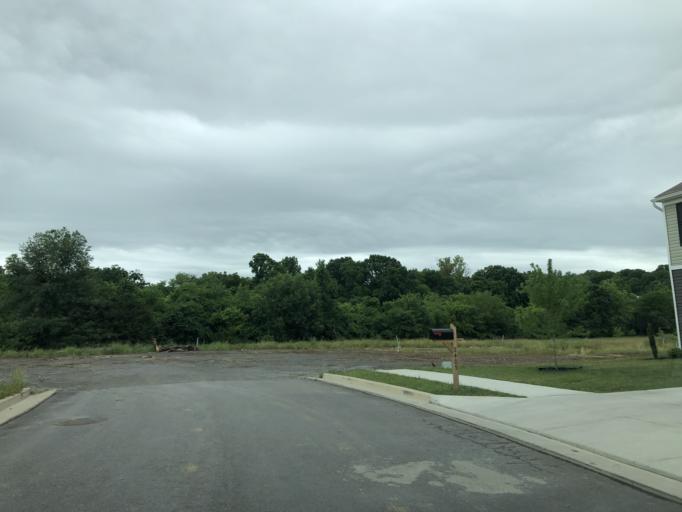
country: US
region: Tennessee
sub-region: Davidson County
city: Goodlettsville
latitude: 36.2564
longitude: -86.7698
